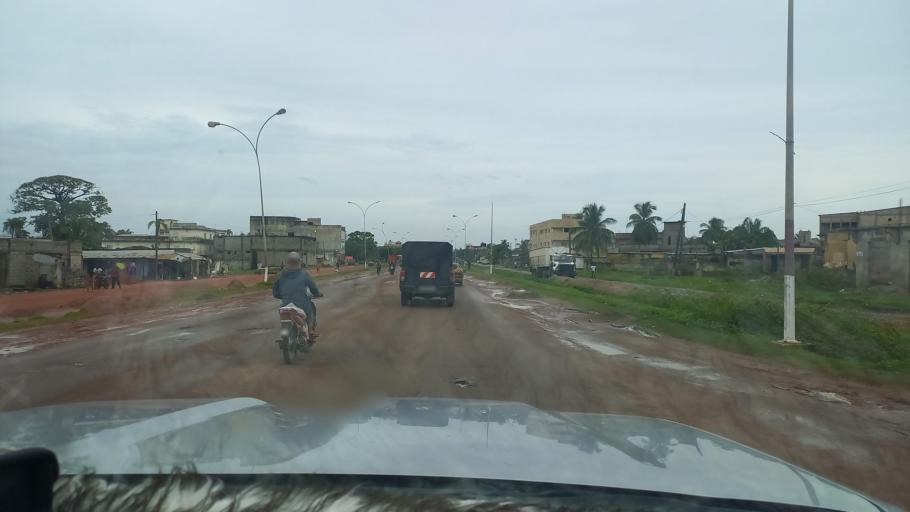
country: SN
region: Ziguinchor
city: Ziguinchor
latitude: 12.5752
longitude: -16.2701
